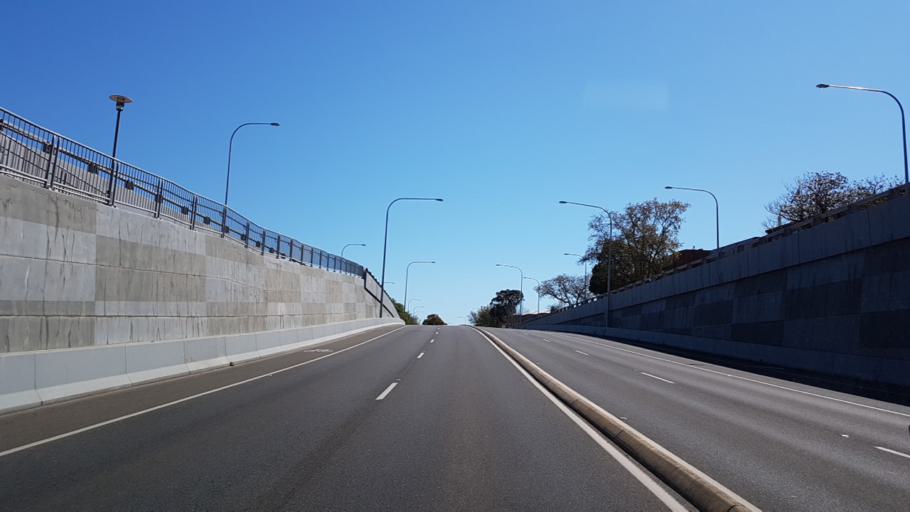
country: AU
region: South Australia
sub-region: City of West Torrens
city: Thebarton
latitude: -34.9234
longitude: 138.5791
